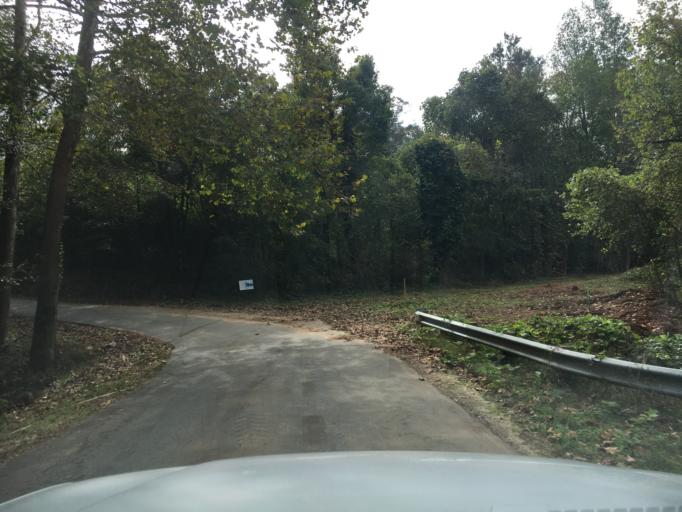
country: US
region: South Carolina
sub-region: Spartanburg County
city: Duncan
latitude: 34.9296
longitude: -82.1401
